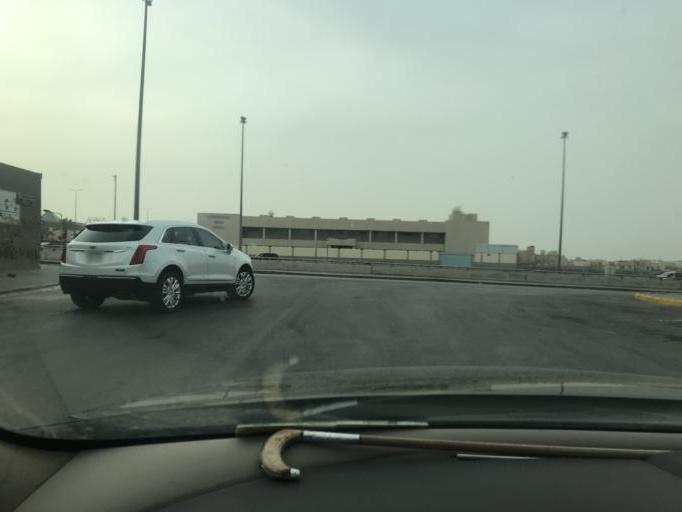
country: SA
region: Ar Riyad
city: Riyadh
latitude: 24.7213
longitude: 46.7739
